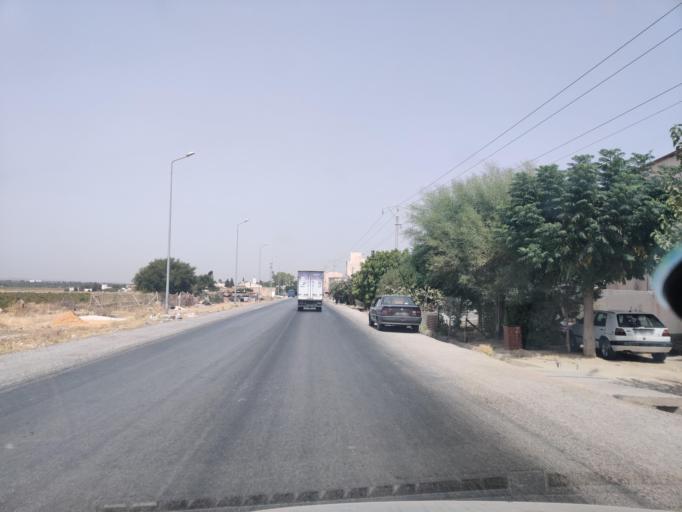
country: TN
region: Tunis
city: La Sebala du Mornag
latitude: 36.6584
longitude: 10.3301
